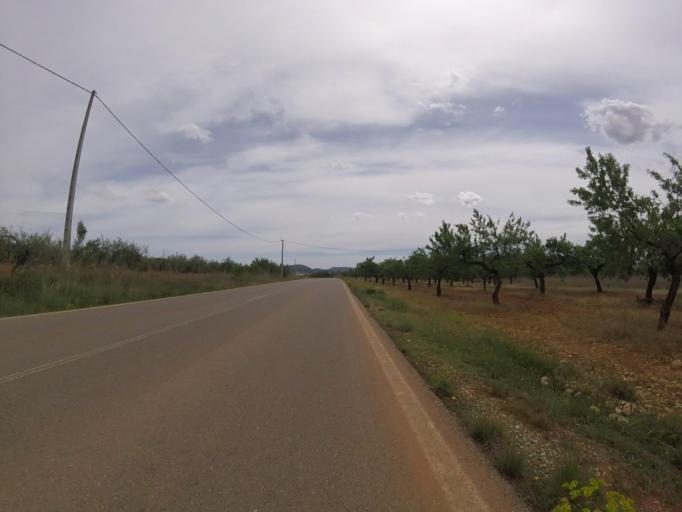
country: ES
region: Valencia
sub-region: Provincia de Castello
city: Cabanes
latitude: 40.1682
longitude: 0.0028
